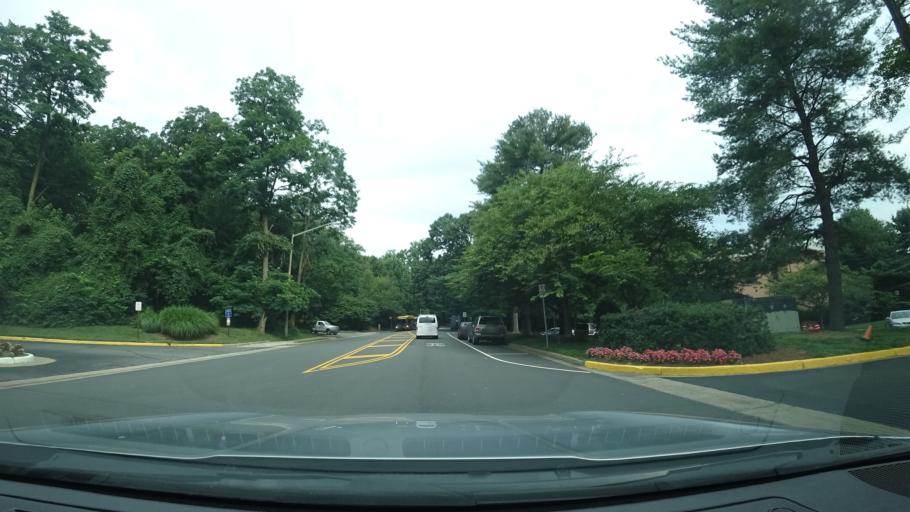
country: US
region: Virginia
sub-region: Fairfax County
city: Reston
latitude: 38.9596
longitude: -77.3497
